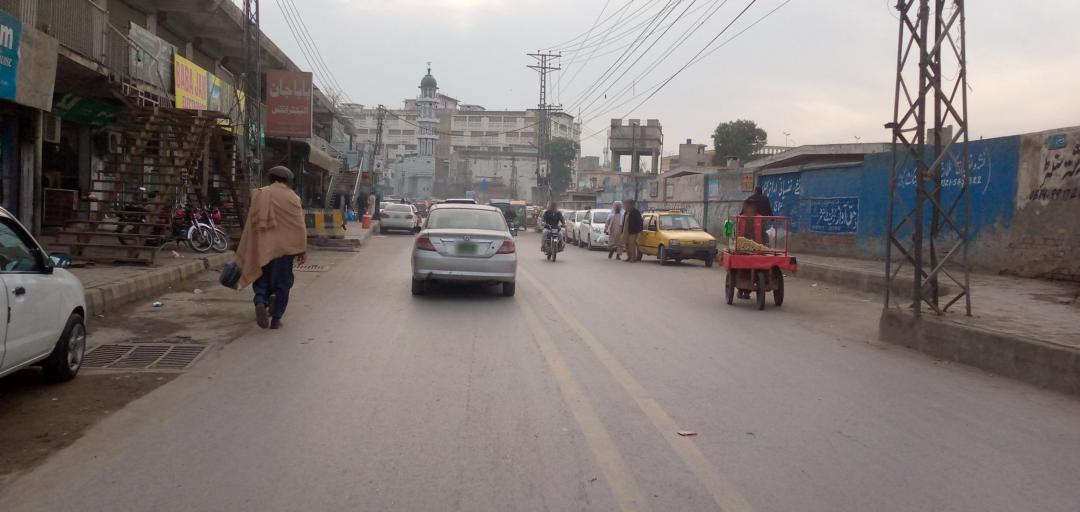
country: PK
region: Khyber Pakhtunkhwa
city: Peshawar
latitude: 34.0058
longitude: 71.5617
